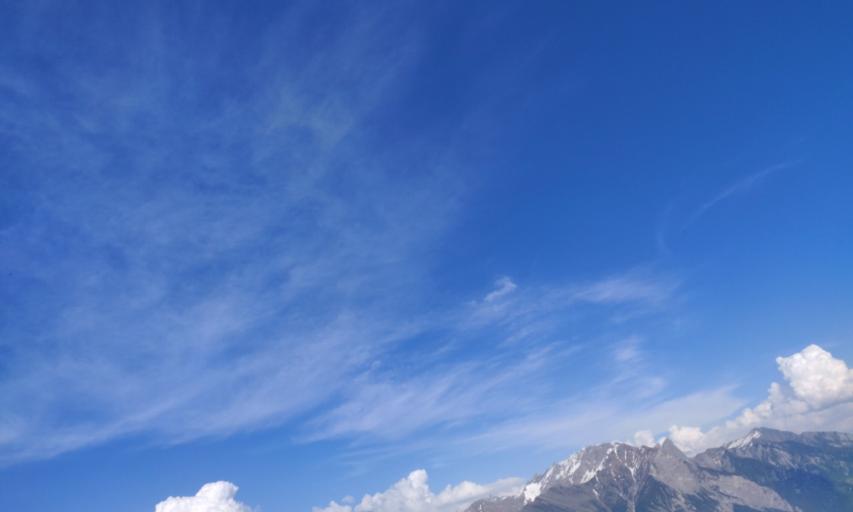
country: CH
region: Saint Gallen
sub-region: Wahlkreis Sarganserland
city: Sargans
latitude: 47.0778
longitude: 9.4364
